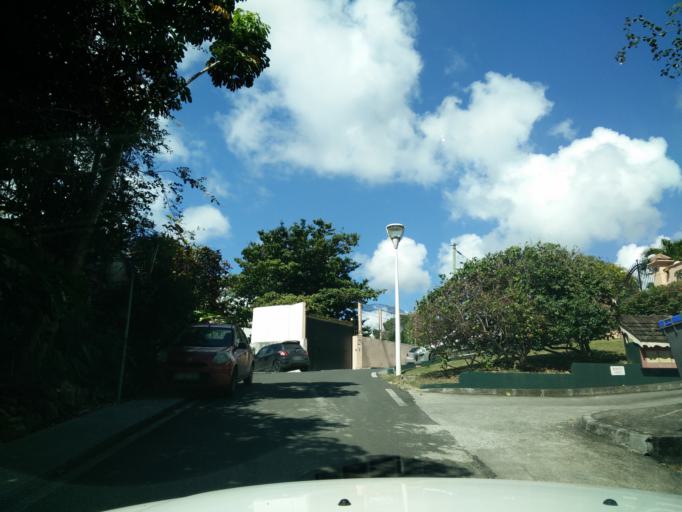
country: GP
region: Guadeloupe
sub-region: Guadeloupe
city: Le Gosier
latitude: 16.2158
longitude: -61.5180
